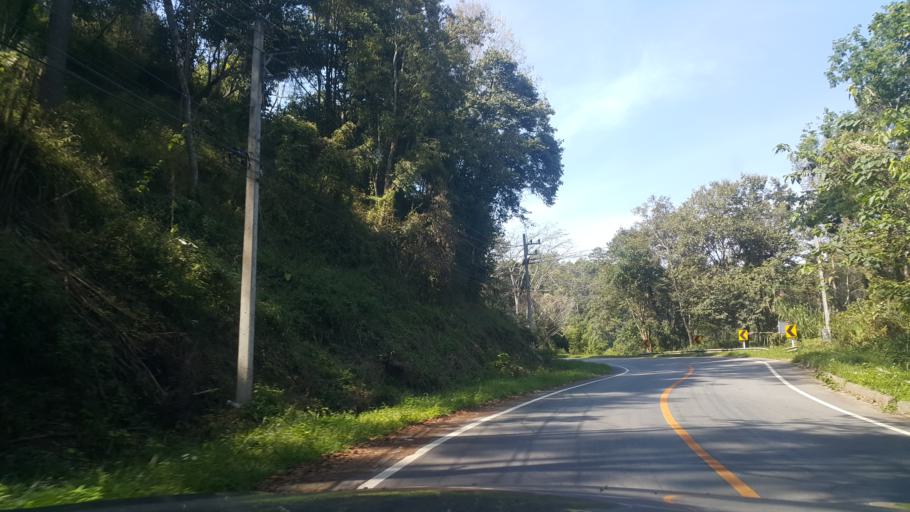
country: TH
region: Chiang Mai
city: Samoeng
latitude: 18.8777
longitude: 98.7888
